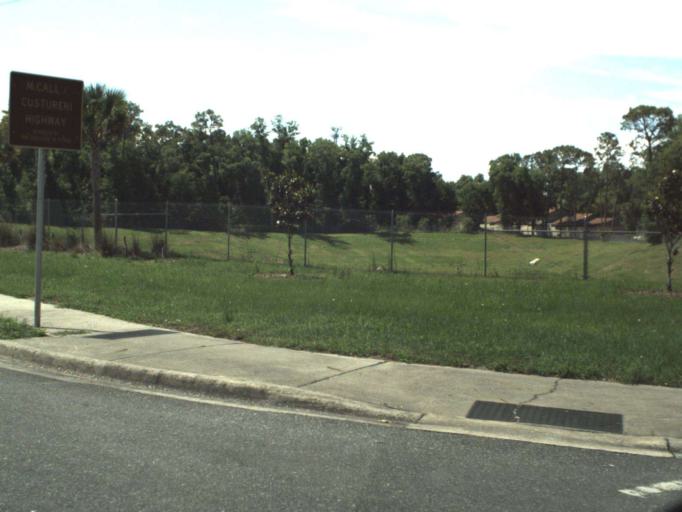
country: US
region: Florida
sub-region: Marion County
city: Ocala
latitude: 29.2011
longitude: -82.0828
